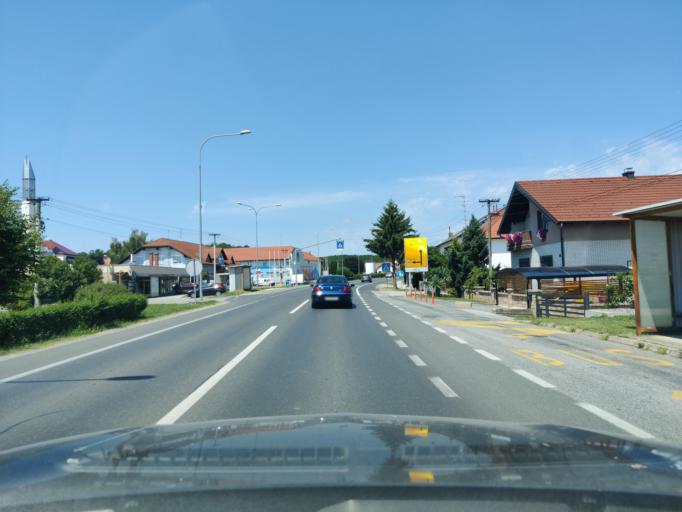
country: HR
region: Medimurska
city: Senkovec
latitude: 46.4029
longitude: 16.4221
